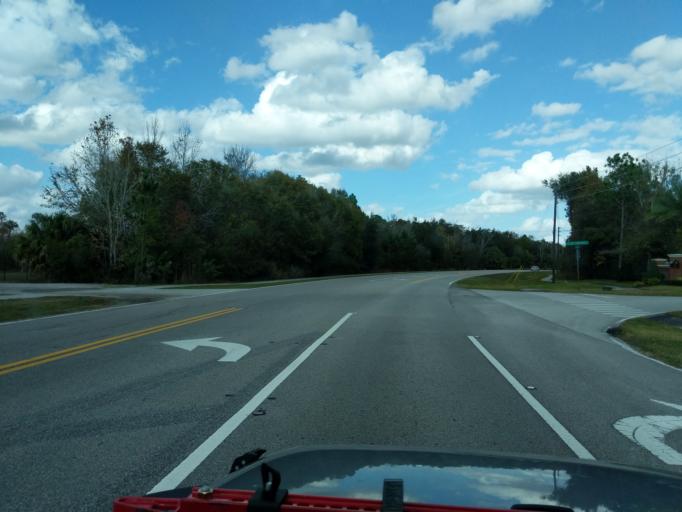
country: US
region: Florida
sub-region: Seminole County
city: Oviedo
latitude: 28.6749
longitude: -81.1753
